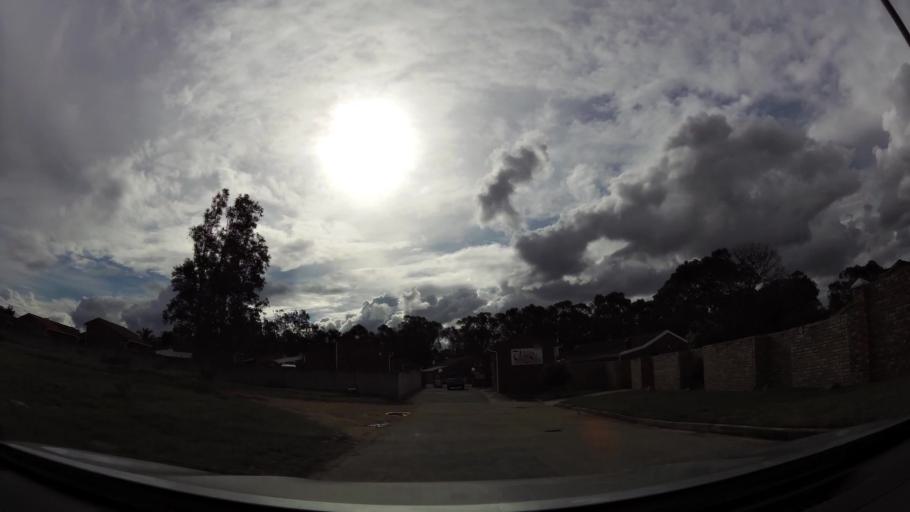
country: ZA
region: Eastern Cape
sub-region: Nelson Mandela Bay Metropolitan Municipality
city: Port Elizabeth
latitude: -33.9352
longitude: 25.4945
